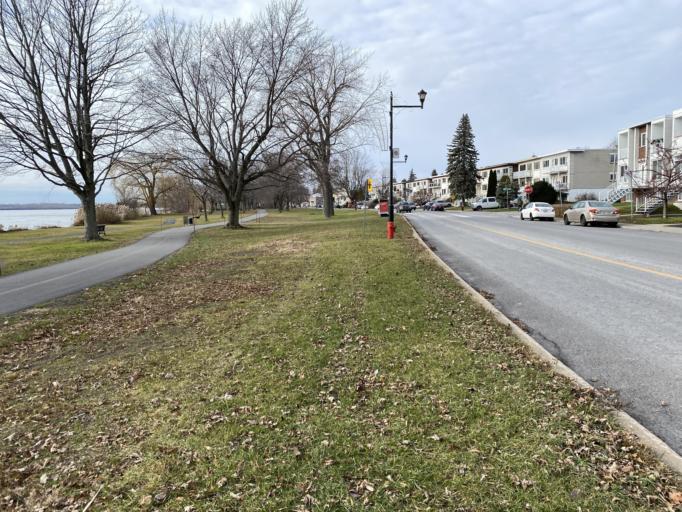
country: CA
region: Quebec
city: Saint-Raymond
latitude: 45.4162
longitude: -73.6120
